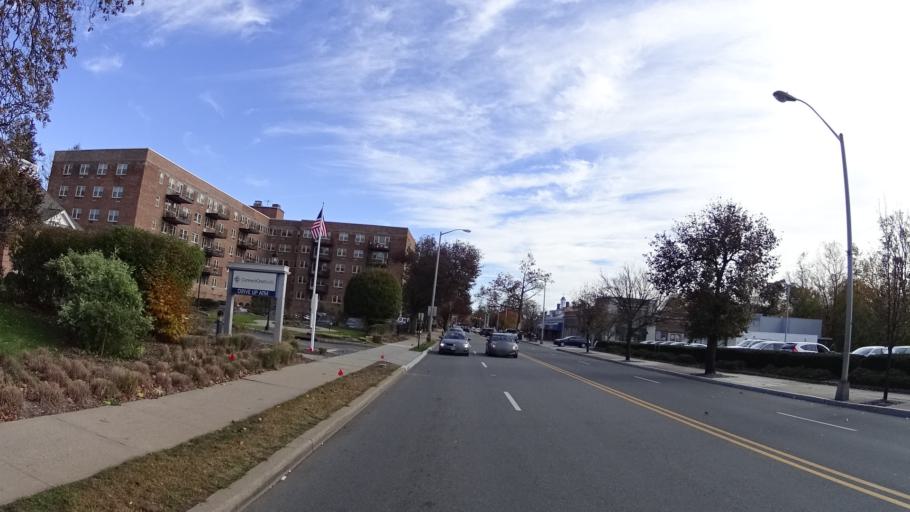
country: US
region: New Jersey
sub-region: Morris County
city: Morristown
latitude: 40.7906
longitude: -74.4743
